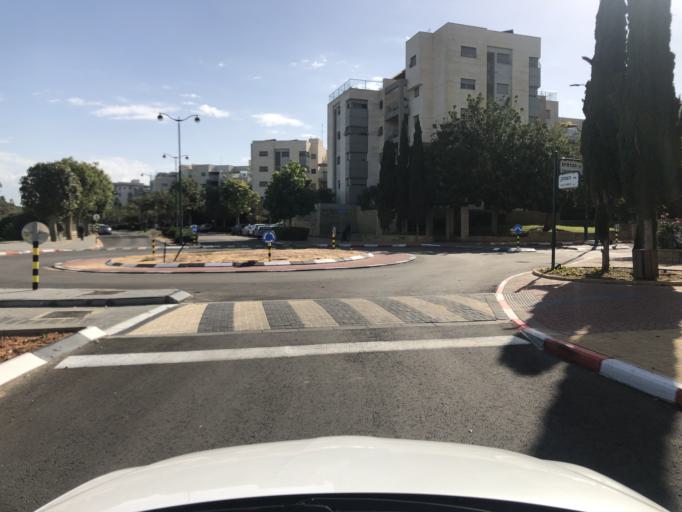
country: IL
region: Central District
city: Ness Ziona
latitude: 31.9158
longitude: 34.7866
